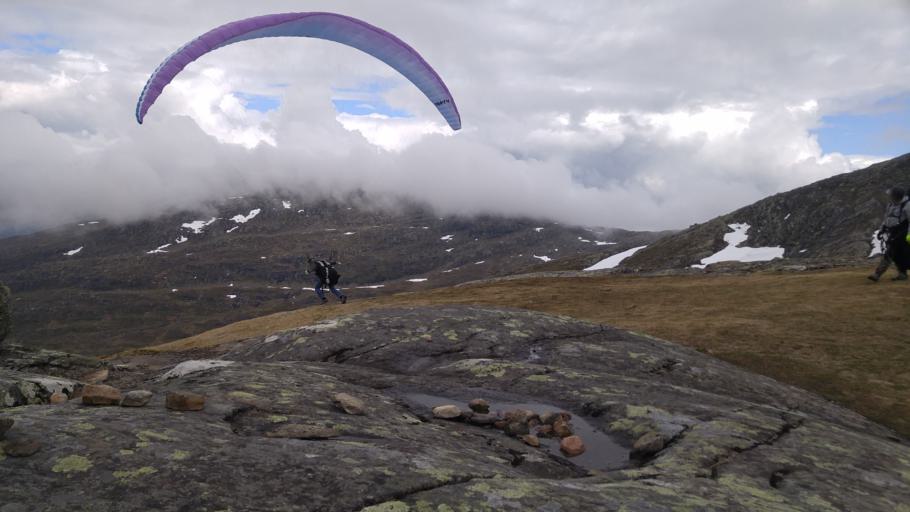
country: SE
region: Jaemtland
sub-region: Are Kommun
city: Are
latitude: 63.4290
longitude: 13.0802
